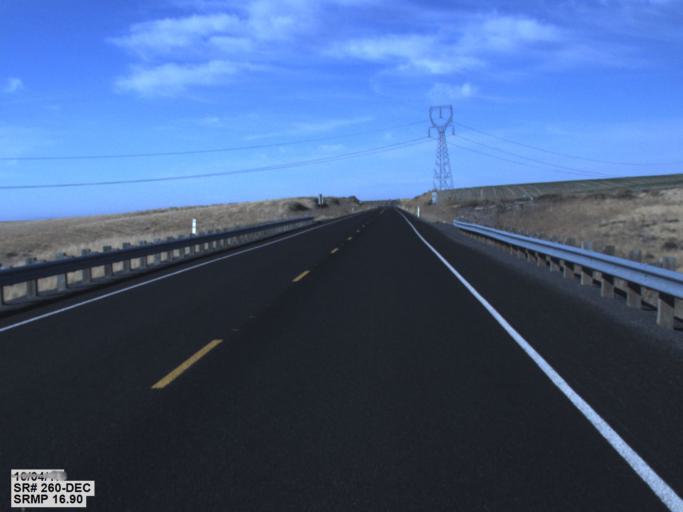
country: US
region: Washington
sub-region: Franklin County
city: Connell
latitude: 46.6201
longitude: -118.7024
